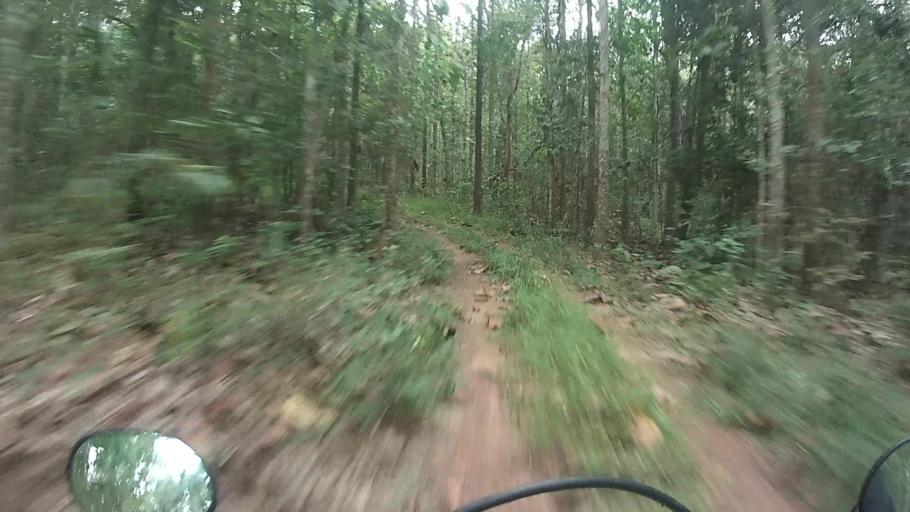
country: TH
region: Chiang Mai
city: Mae On
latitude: 18.8868
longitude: 99.2058
